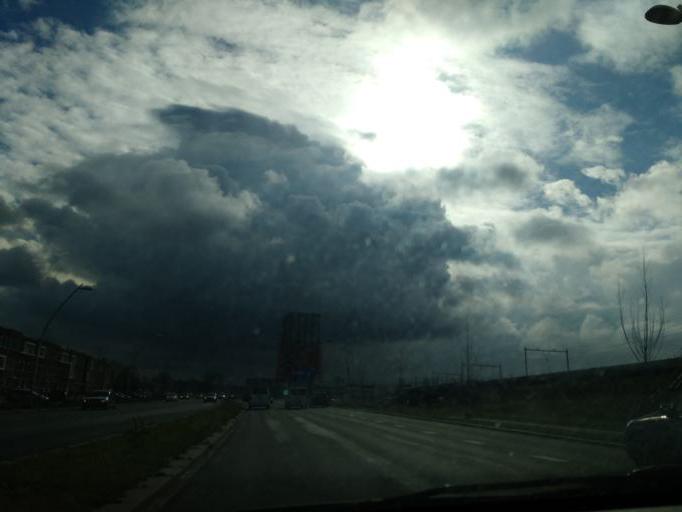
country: NL
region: Gelderland
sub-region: Gemeente Nijmegen
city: Nijmegen
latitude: 51.8661
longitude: 5.8601
